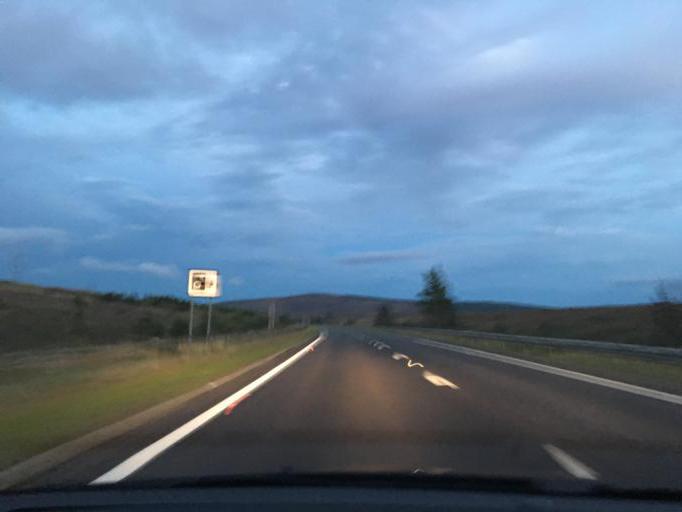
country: GB
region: Scotland
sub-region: Highland
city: Kingussie
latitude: 56.8141
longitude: -4.1249
